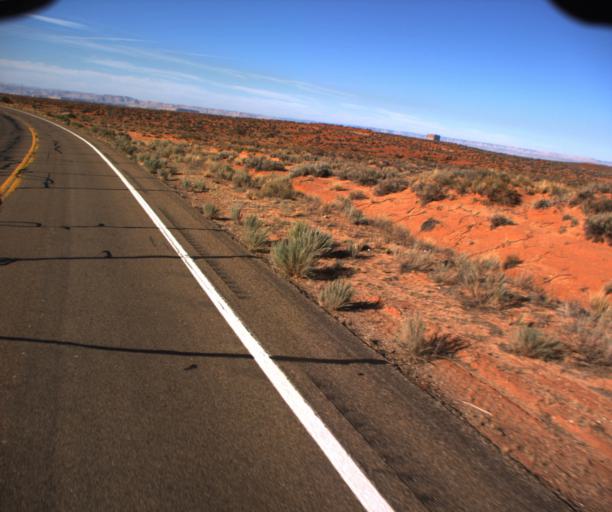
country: US
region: Arizona
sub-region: Coconino County
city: LeChee
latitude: 36.8764
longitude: -111.3435
